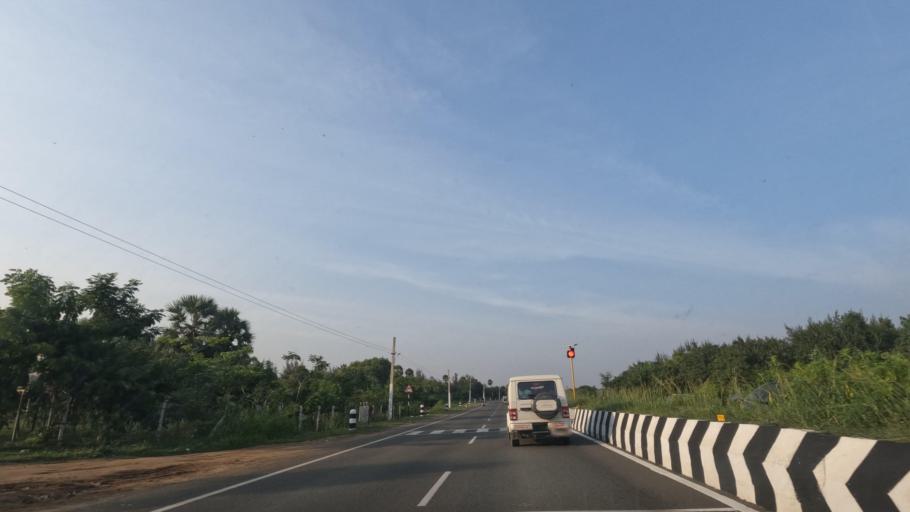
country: IN
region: Tamil Nadu
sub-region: Kancheepuram
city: Mamallapuram
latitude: 12.6658
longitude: 80.2096
